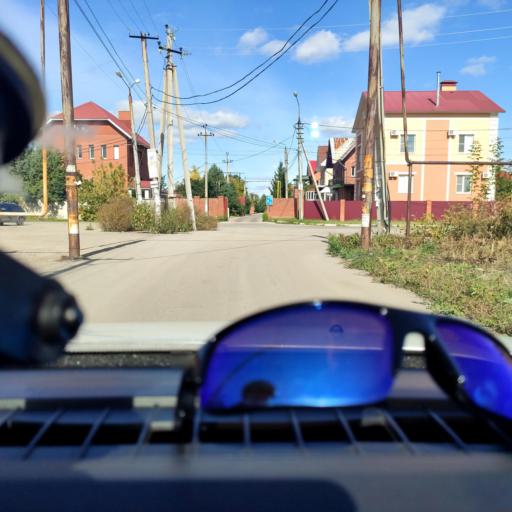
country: RU
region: Samara
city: Samara
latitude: 53.1517
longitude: 50.0825
